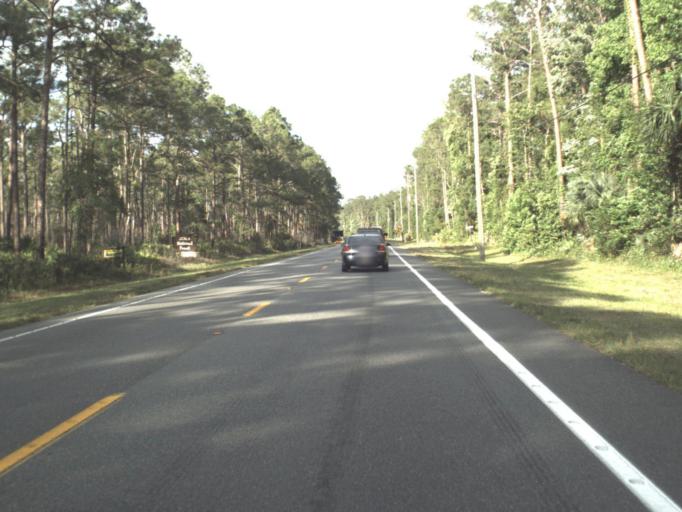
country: US
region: Florida
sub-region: Lake County
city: Astor
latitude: 29.1558
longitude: -81.5625
